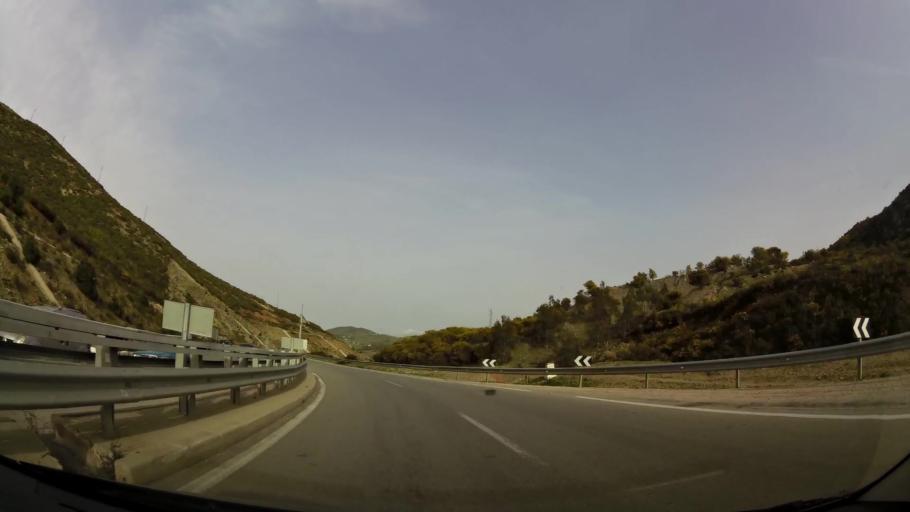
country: MA
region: Tanger-Tetouan
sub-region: Tetouan
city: Saddina
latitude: 35.5485
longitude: -5.5347
